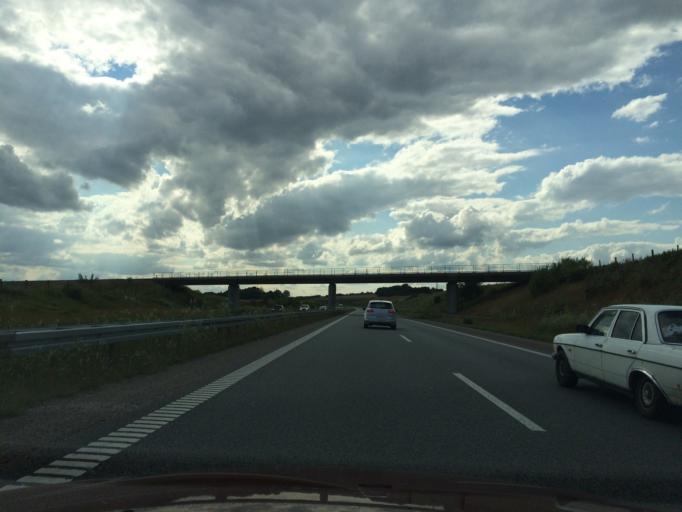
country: DK
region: Central Jutland
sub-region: Arhus Kommune
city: Lystrup
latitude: 56.2223
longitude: 10.2093
